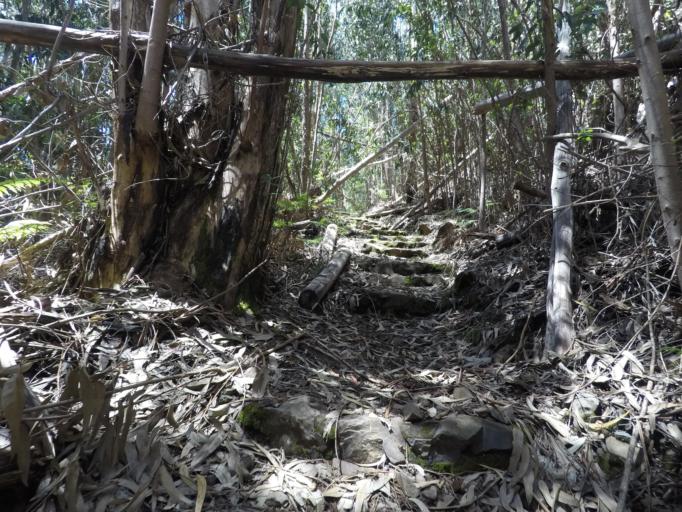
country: PT
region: Madeira
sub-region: Camara de Lobos
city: Curral das Freiras
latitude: 32.7482
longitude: -16.9693
